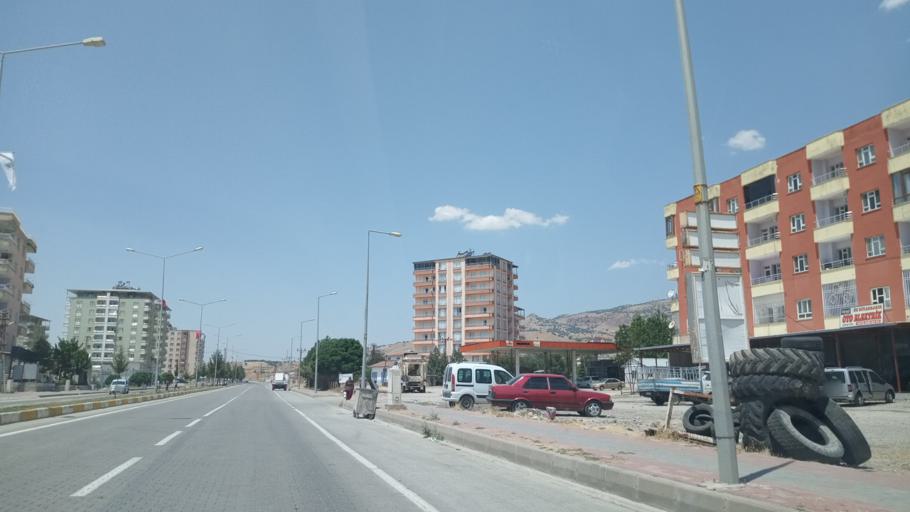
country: TR
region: Batman
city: Kozluk
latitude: 38.1676
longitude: 41.4933
